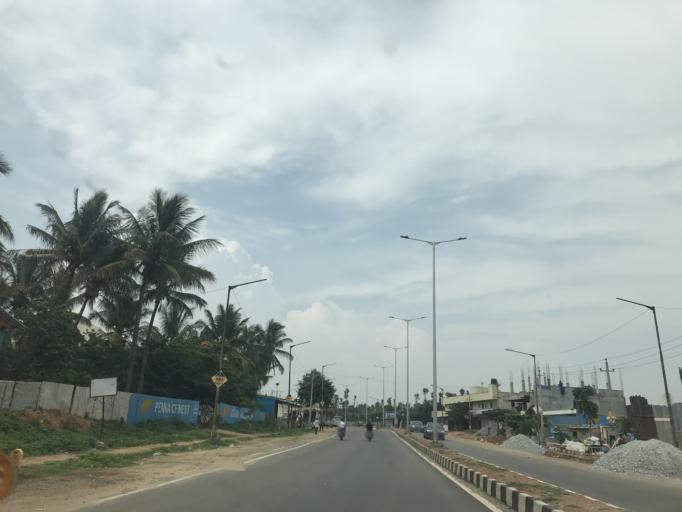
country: IN
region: Karnataka
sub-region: Bangalore Urban
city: Yelahanka
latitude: 13.1018
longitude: 77.6583
